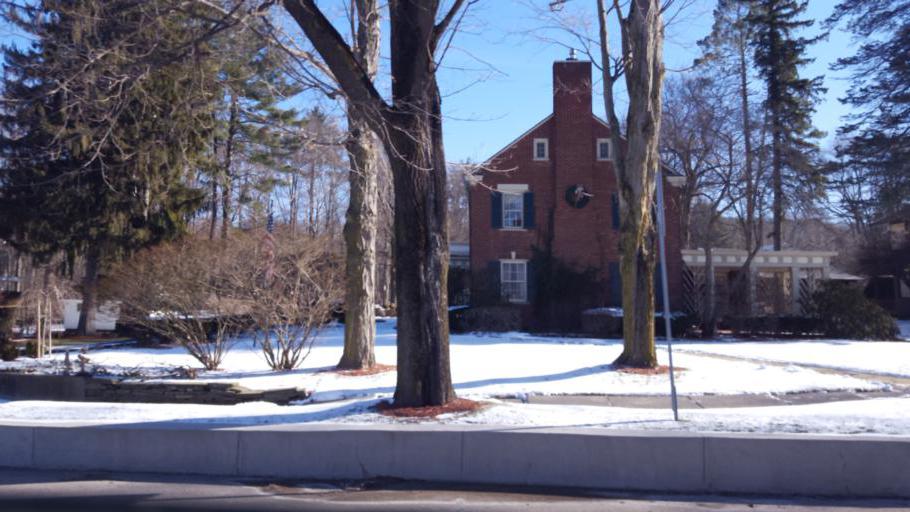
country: US
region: New York
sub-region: Allegany County
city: Wellsville
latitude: 42.1287
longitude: -77.9587
